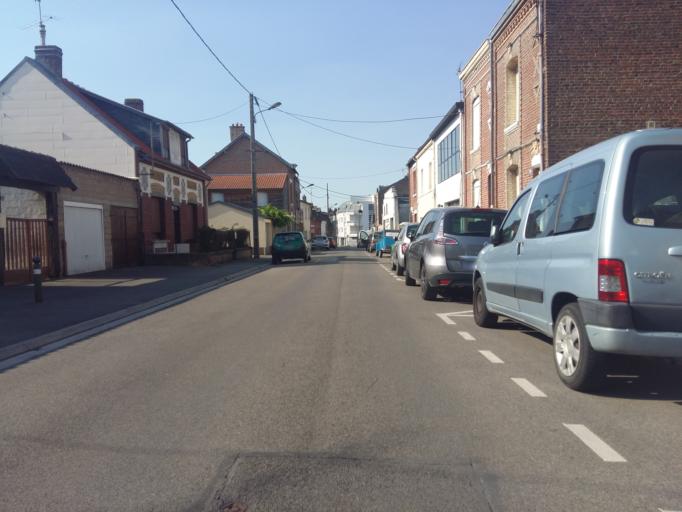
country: FR
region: Picardie
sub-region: Departement de la Somme
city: Rivery
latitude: 49.9064
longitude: 2.3211
